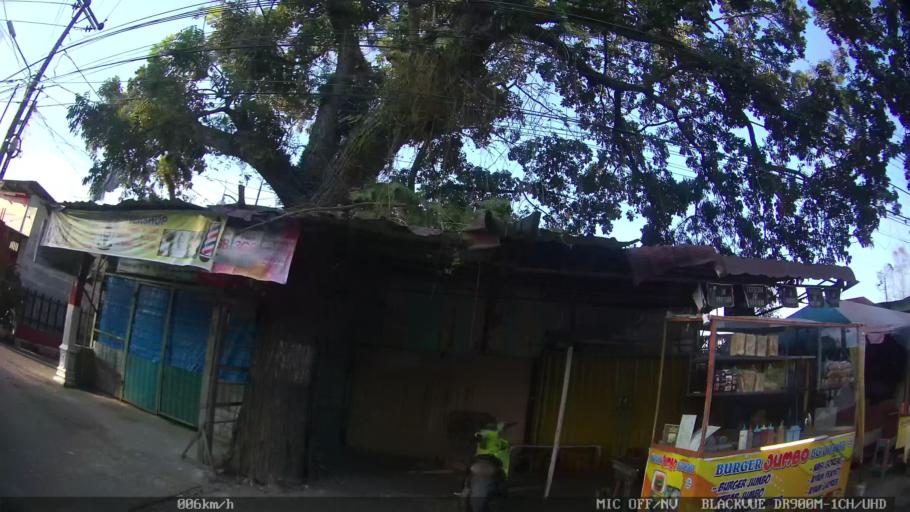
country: ID
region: North Sumatra
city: Medan
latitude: 3.6241
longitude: 98.6647
